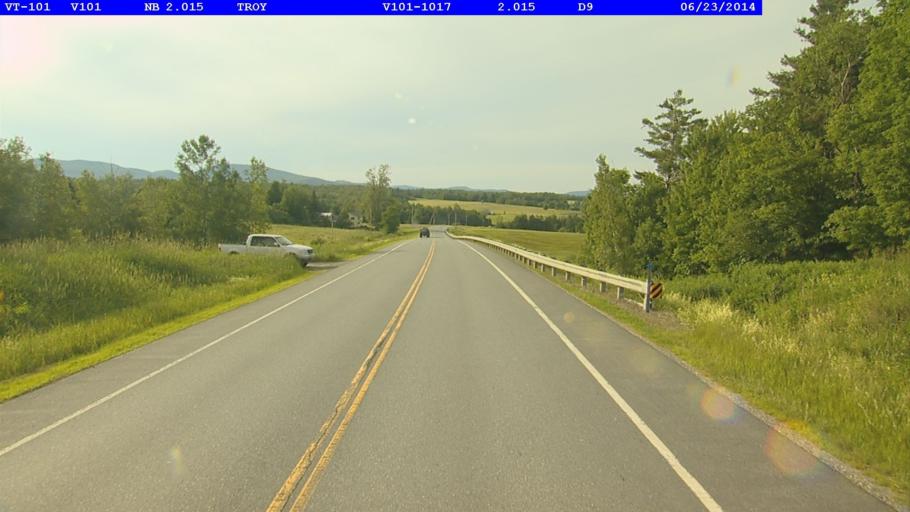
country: US
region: Vermont
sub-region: Orleans County
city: Newport
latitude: 44.9321
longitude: -72.4096
